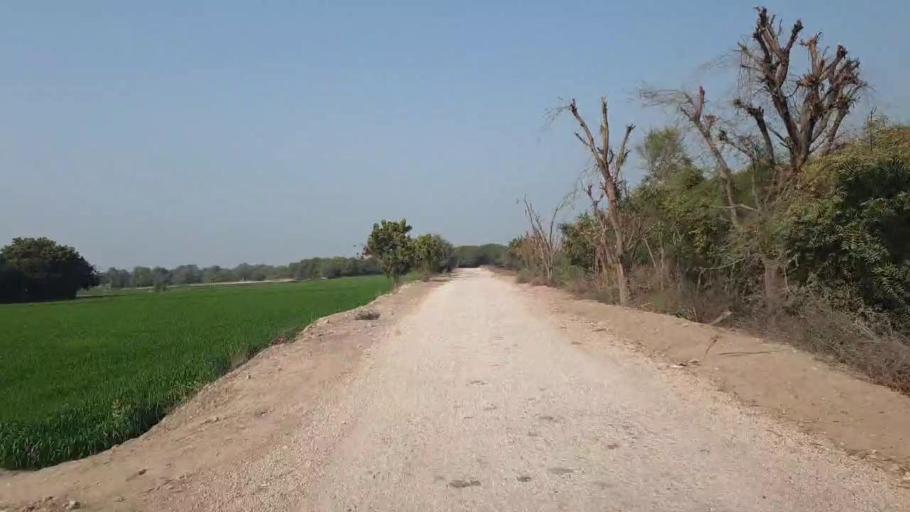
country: PK
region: Sindh
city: Hala
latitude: 25.8705
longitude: 68.4619
